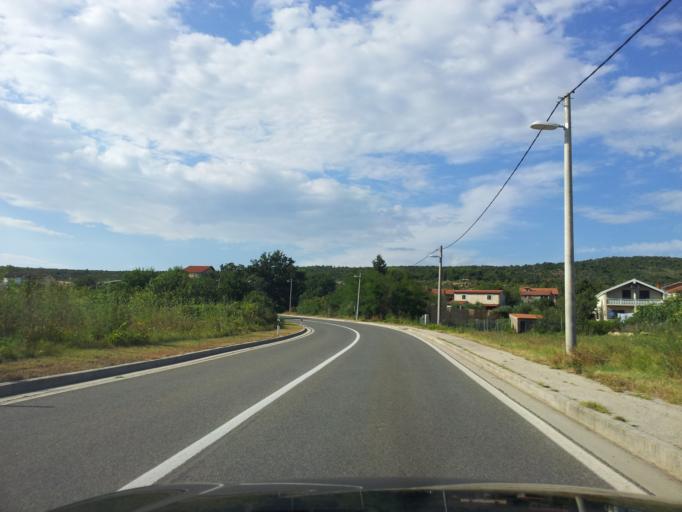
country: HR
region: Zadarska
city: Posedarje
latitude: 44.2139
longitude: 15.4686
